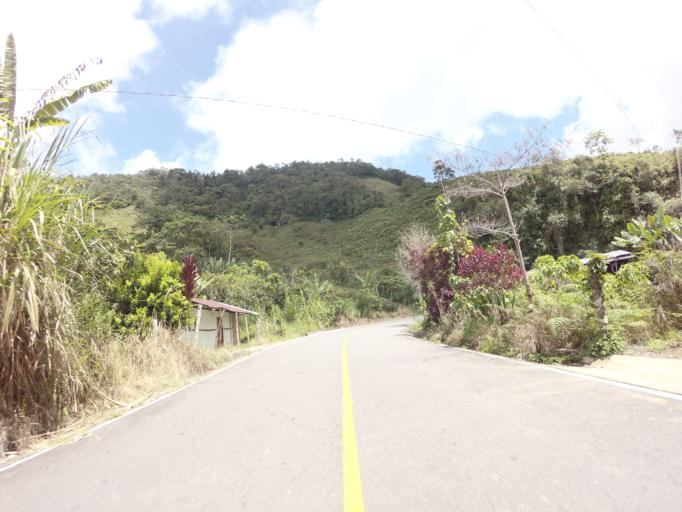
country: CO
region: Caldas
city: Marquetalia
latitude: 5.2764
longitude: -75.1095
